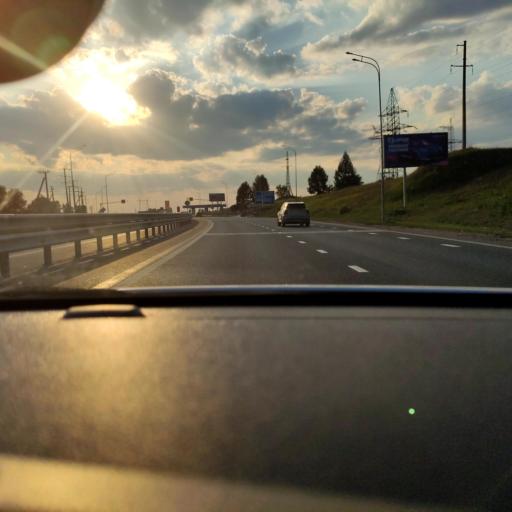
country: RU
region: Tatarstan
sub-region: Gorod Kazan'
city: Kazan
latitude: 55.9161
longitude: 49.1574
